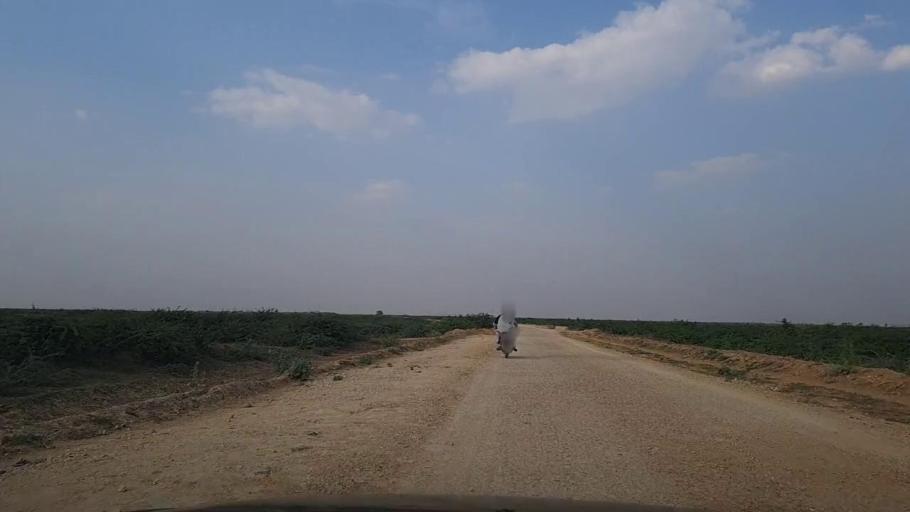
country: PK
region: Sindh
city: Gharo
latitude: 24.8223
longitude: 67.7446
